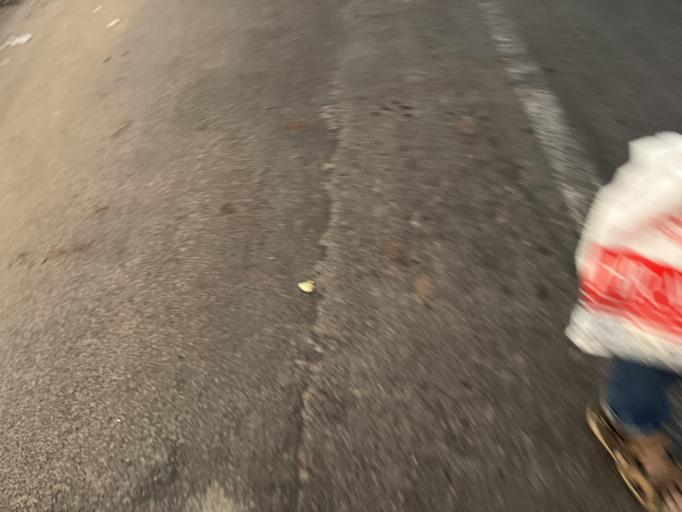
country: IN
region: Odisha
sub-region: Cuttack
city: Cuttack
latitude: 20.4027
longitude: 85.8805
